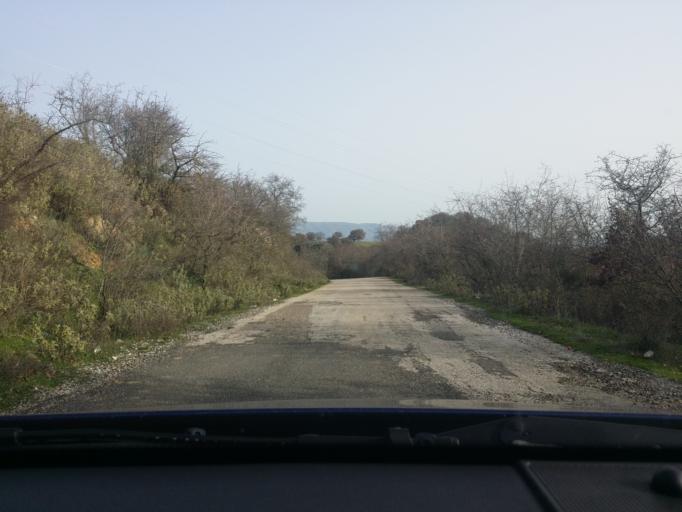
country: GR
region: West Greece
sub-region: Nomos Aitolias kai Akarnanias
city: Katouna
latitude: 38.8087
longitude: 21.0910
